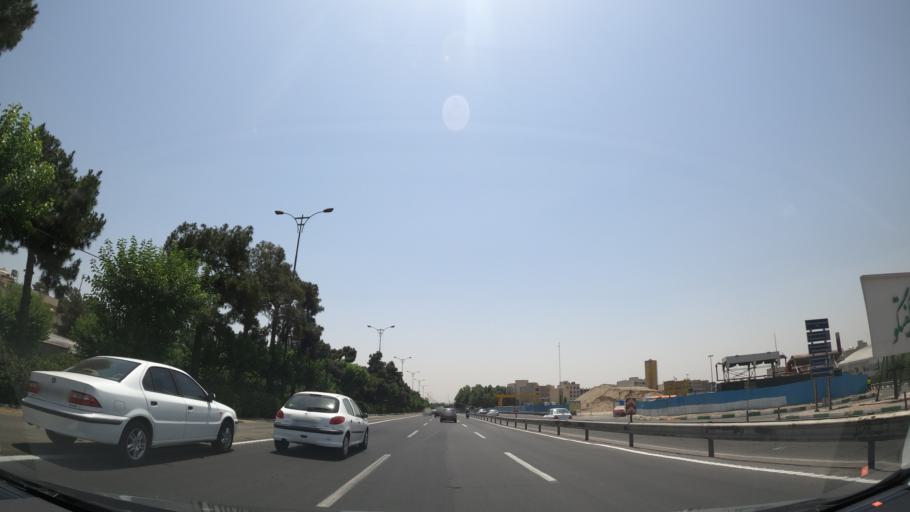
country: IR
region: Tehran
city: Tehran
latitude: 35.7337
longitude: 51.3833
